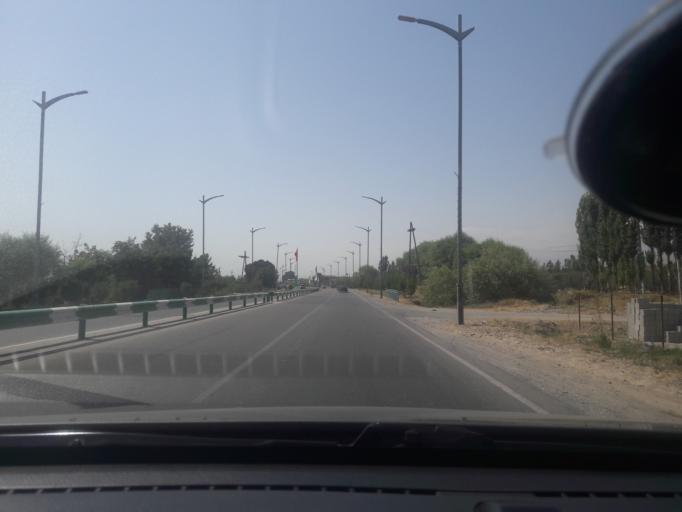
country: TJ
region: Republican Subordination
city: Hisor
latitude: 38.5609
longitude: 68.4475
